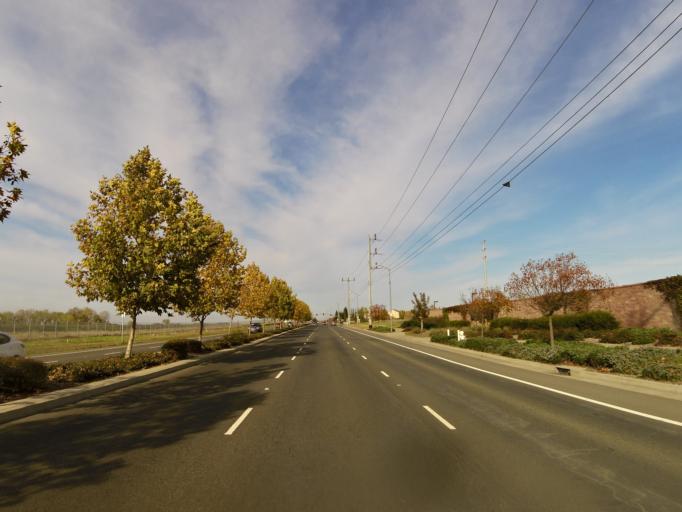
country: US
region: California
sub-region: Sacramento County
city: Rancho Cordova
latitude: 38.5454
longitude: -121.2427
